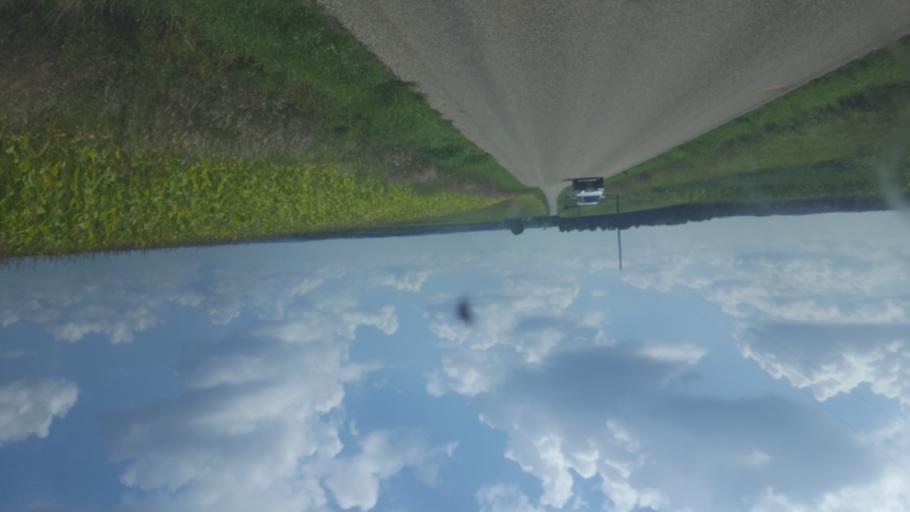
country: US
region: Ohio
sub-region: Knox County
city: Oak Hill
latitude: 40.3817
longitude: -82.2990
